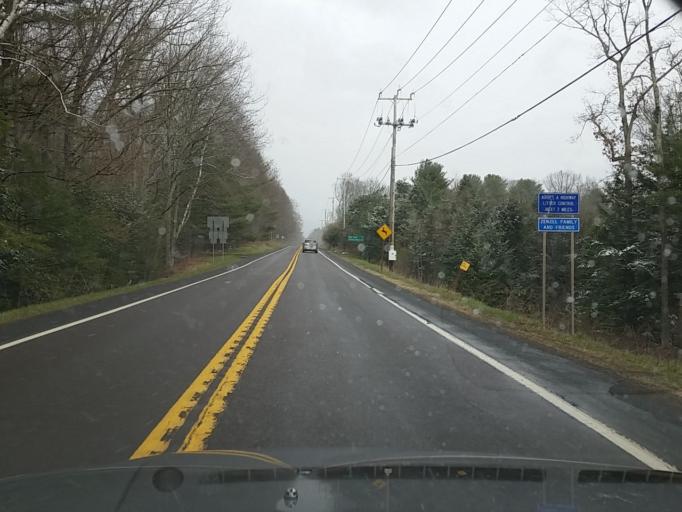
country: US
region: Pennsylvania
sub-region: Sullivan County
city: Laporte
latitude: 41.2727
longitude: -76.4506
